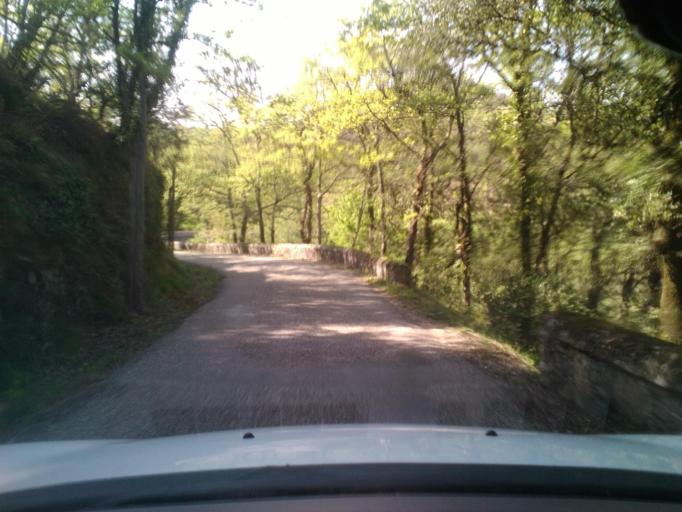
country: FR
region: Languedoc-Roussillon
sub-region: Departement du Gard
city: Lasalle
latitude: 44.0197
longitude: 3.8748
